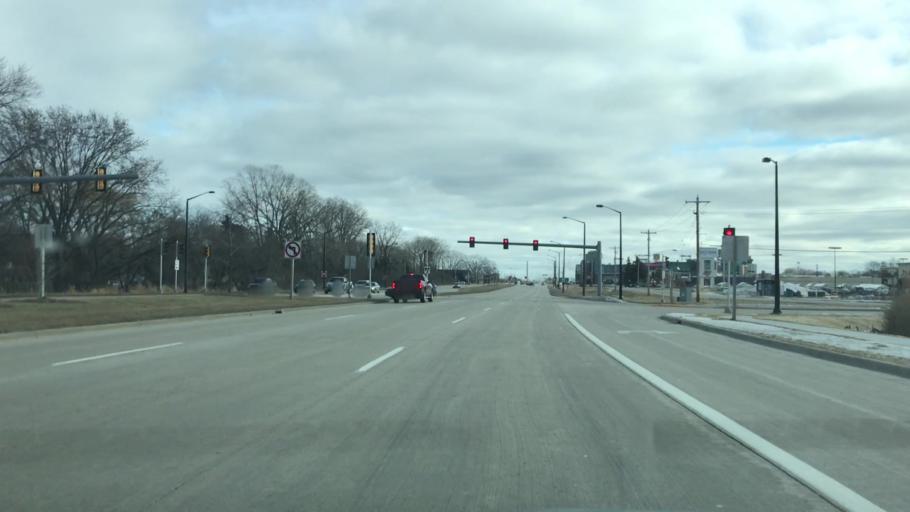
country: US
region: Wisconsin
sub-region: Brown County
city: Ashwaubenon
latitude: 44.5085
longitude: -88.0776
